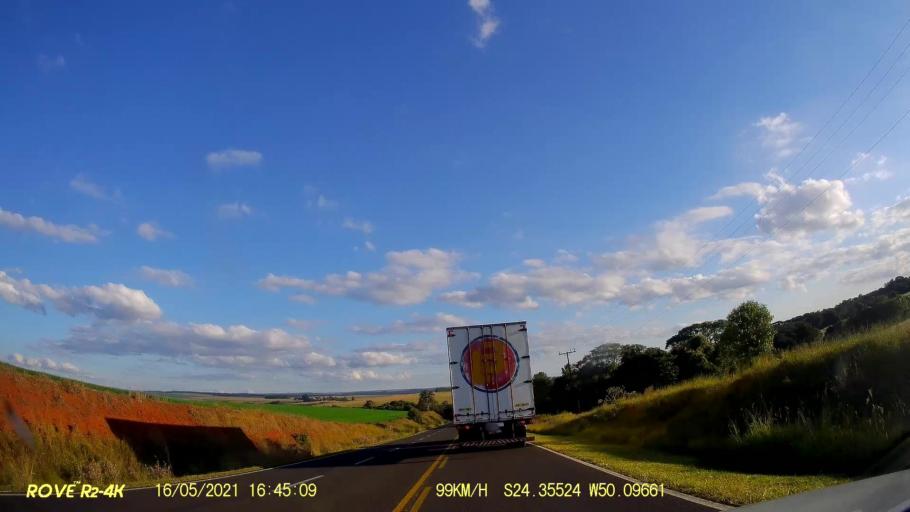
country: BR
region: Parana
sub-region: Pirai Do Sul
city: Pirai do Sul
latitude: -24.3556
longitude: -50.0966
